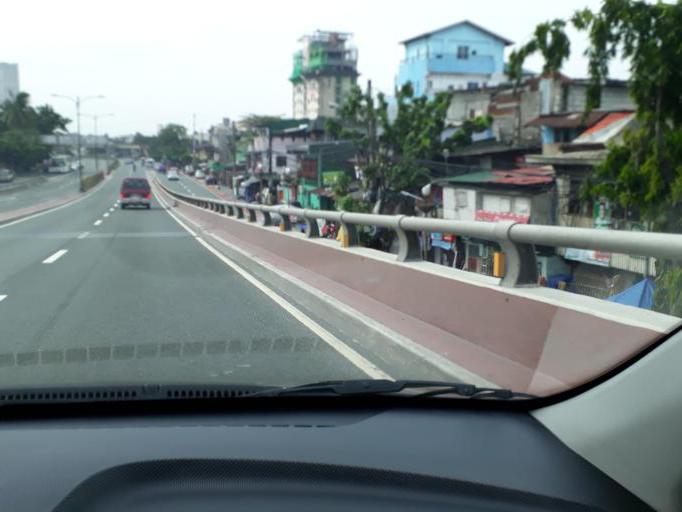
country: PH
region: Metro Manila
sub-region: City of Manila
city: Quiapo
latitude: 14.6024
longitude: 120.9987
